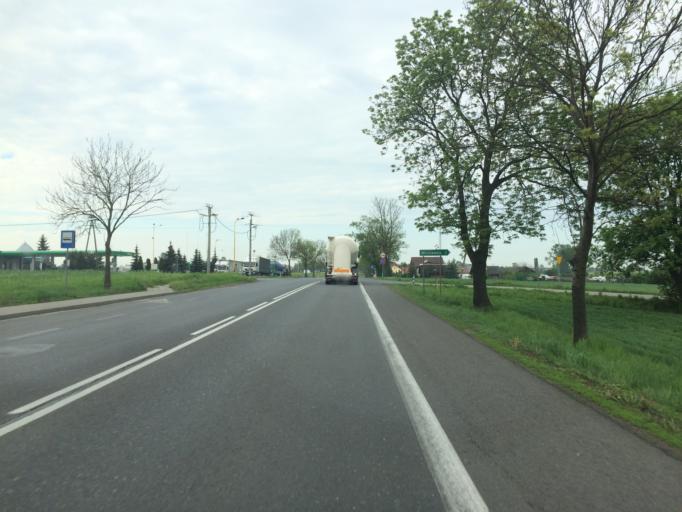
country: PL
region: Masovian Voivodeship
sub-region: Powiat mlawski
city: Wisniewo
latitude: 53.0762
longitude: 20.3526
